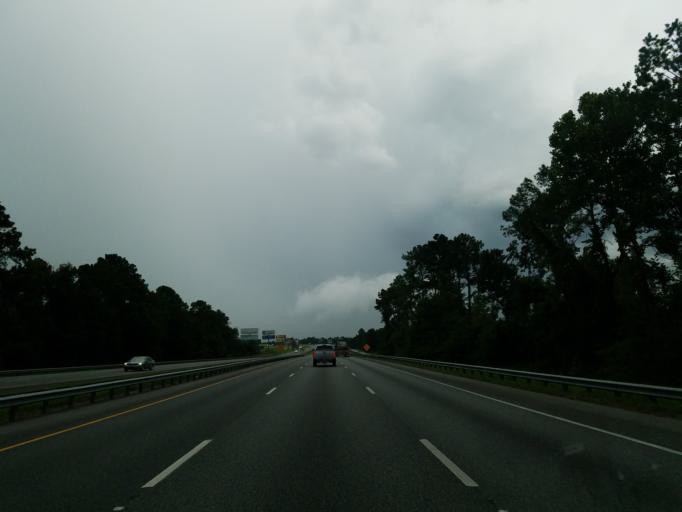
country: US
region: Georgia
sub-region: Lowndes County
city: Valdosta
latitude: 30.7088
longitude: -83.2497
